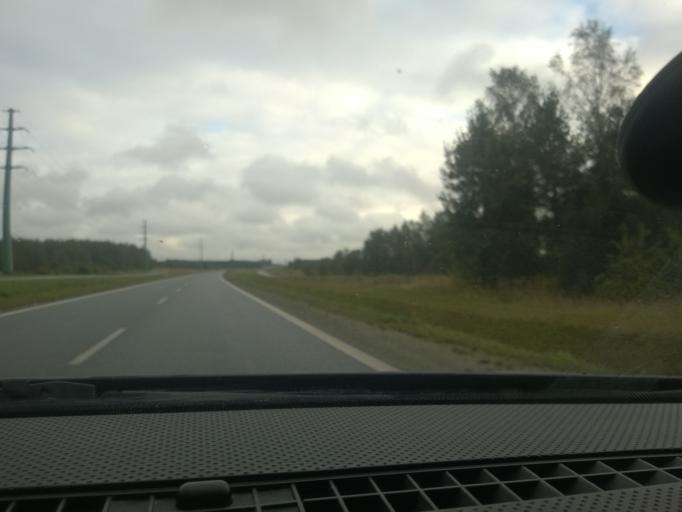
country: PL
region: Lodz Voivodeship
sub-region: Powiat sieradzki
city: Sieradz
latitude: 51.5802
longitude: 18.6763
